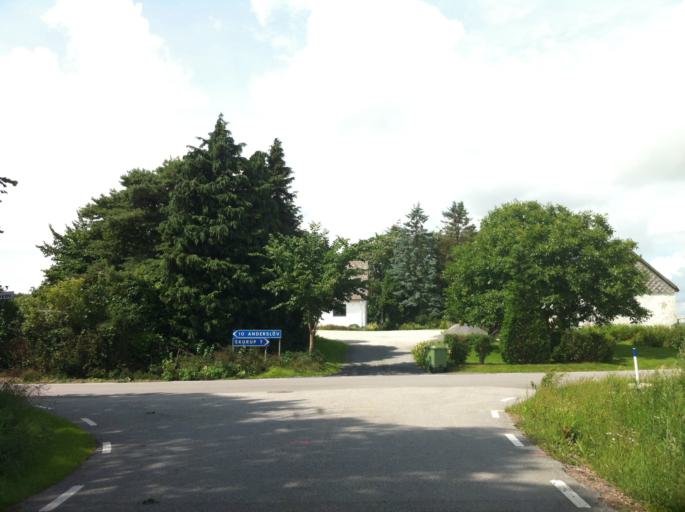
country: SE
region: Skane
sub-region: Skurups Kommun
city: Skurup
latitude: 55.4178
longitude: 13.4638
